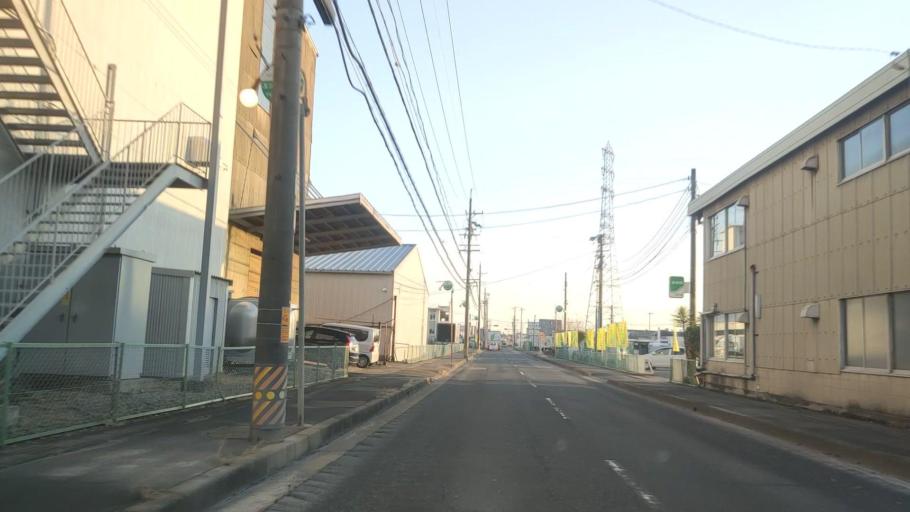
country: JP
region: Gifu
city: Kasamatsucho
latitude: 35.3849
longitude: 136.7821
